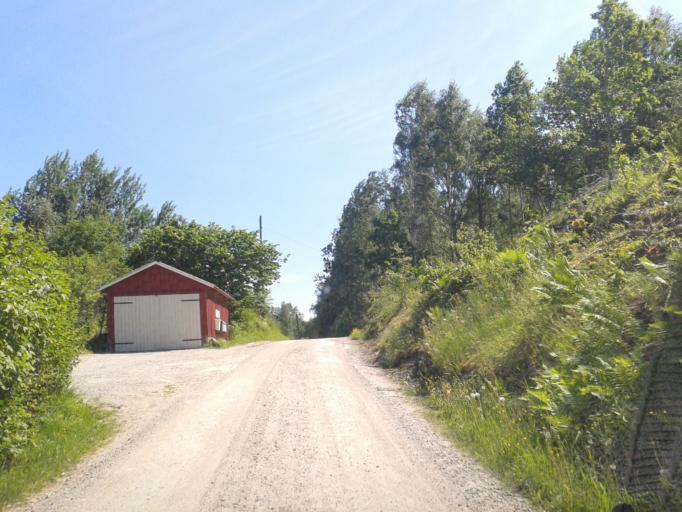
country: SE
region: Vaestra Goetaland
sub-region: Stromstads Kommun
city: Stroemstad
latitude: 58.8624
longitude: 11.2230
